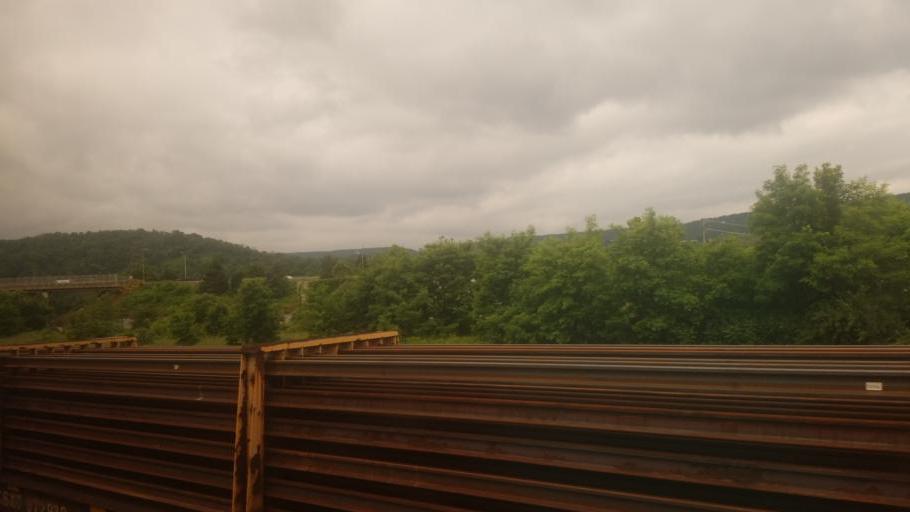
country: US
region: Maryland
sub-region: Allegany County
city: Cumberland
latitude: 39.6445
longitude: -78.7610
